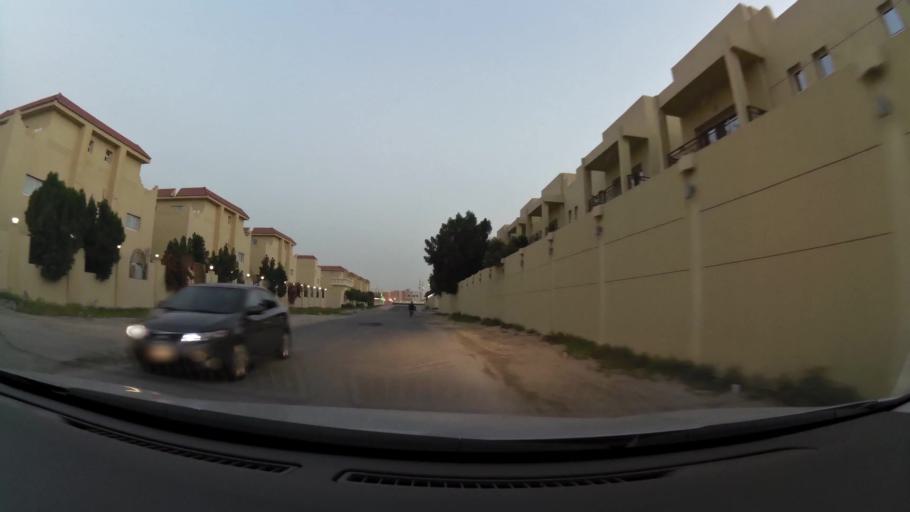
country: QA
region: Baladiyat ar Rayyan
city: Ar Rayyan
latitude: 25.2589
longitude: 51.4608
